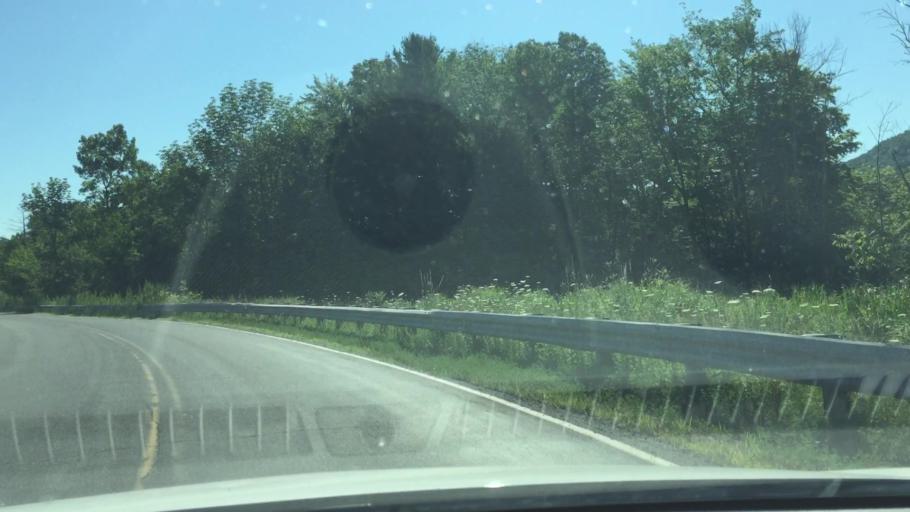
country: US
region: Massachusetts
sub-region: Berkshire County
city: Pittsfield
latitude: 42.4222
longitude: -73.3024
